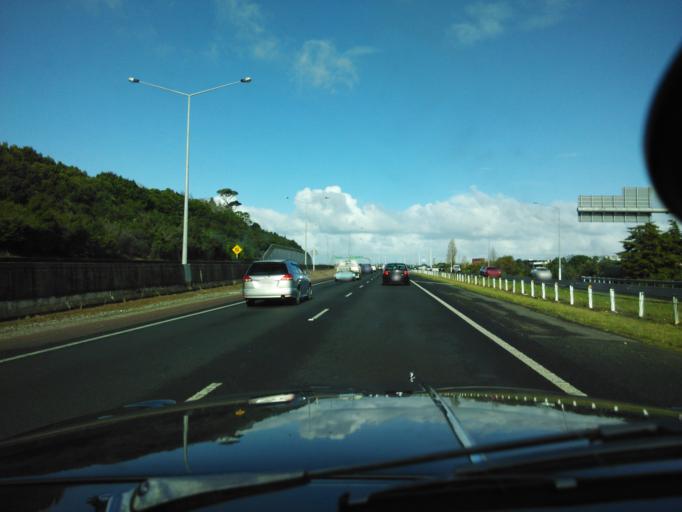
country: NZ
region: Auckland
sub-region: Auckland
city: North Shore
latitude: -36.7660
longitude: 174.7401
